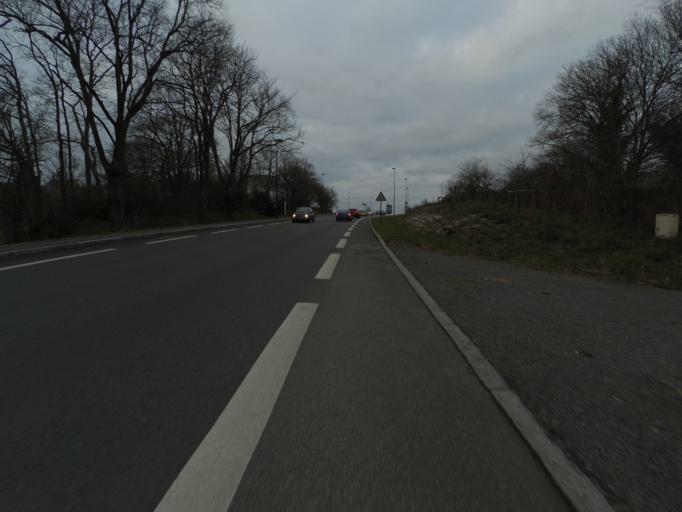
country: FR
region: Pays de la Loire
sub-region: Departement de la Loire-Atlantique
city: Carquefou
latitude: 47.3057
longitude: -1.4836
